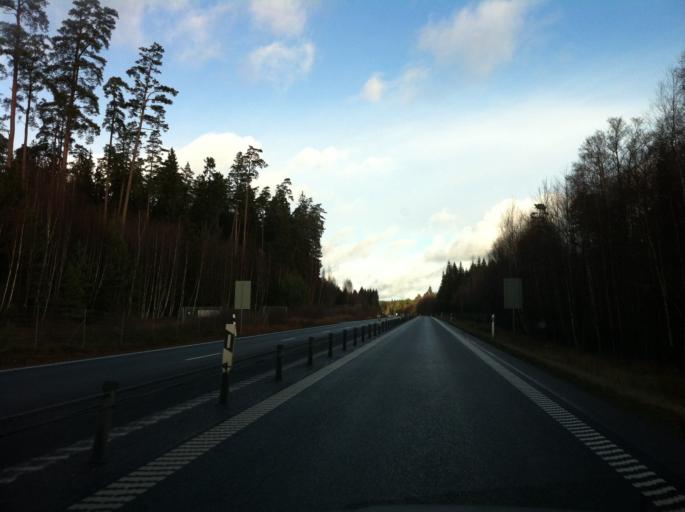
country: SE
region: Skane
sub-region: Osby Kommun
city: Osby
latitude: 56.4083
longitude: 14.0441
